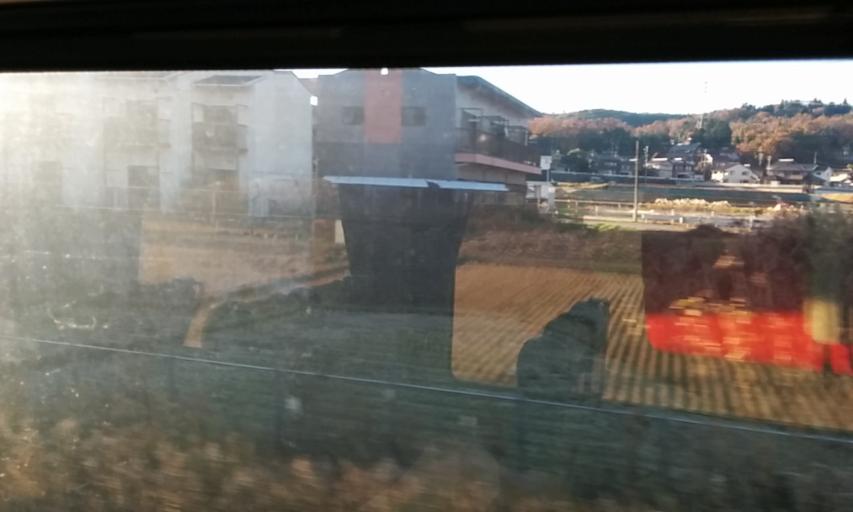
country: JP
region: Gifu
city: Mizunami
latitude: 35.3745
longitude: 137.2616
